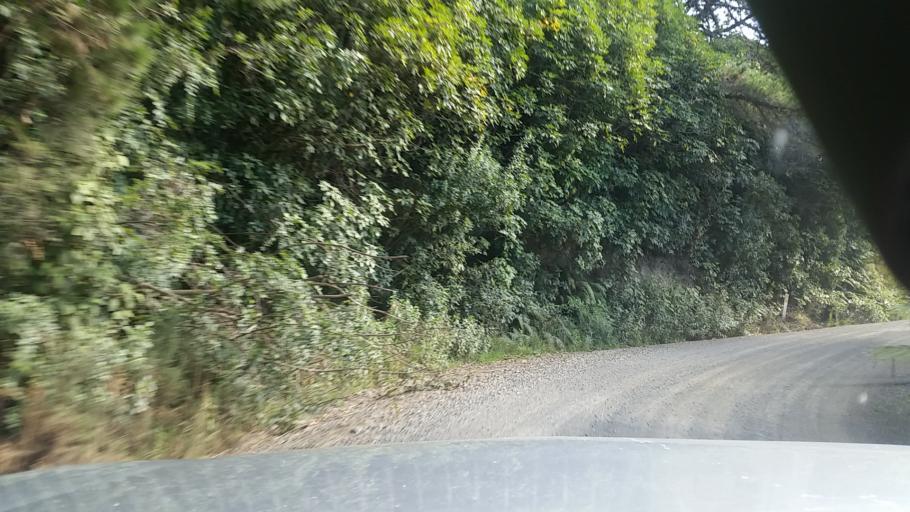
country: NZ
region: Marlborough
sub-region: Marlborough District
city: Picton
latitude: -41.2976
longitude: 174.1235
